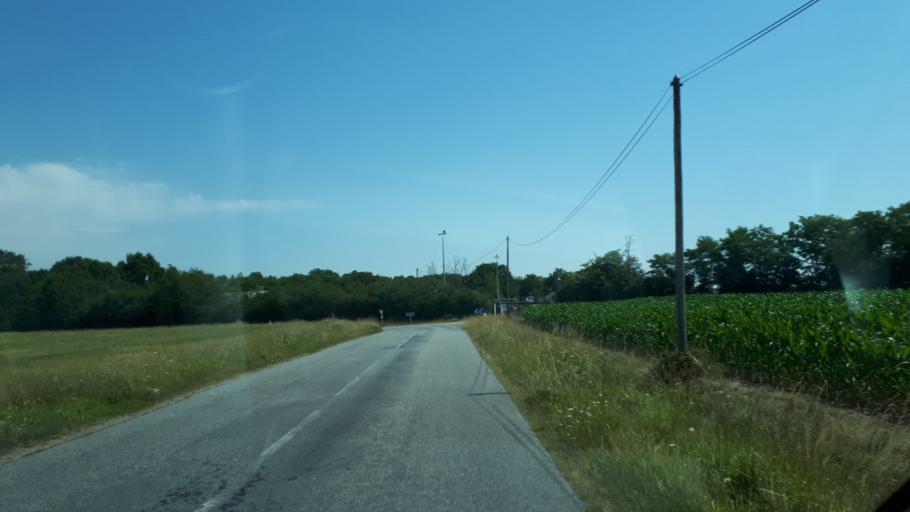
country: FR
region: Centre
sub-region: Departement d'Eure-et-Loir
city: Arrou
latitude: 48.0740
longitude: 1.1234
